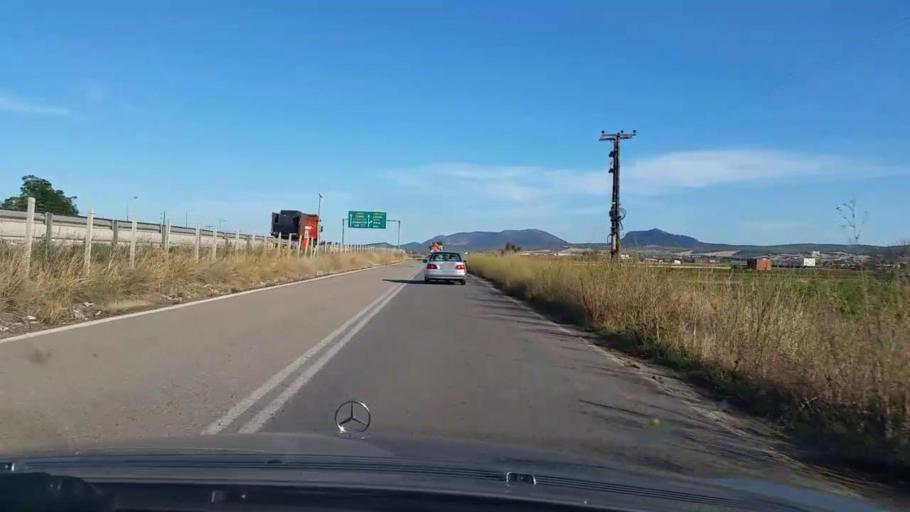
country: GR
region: Central Greece
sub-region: Nomos Voiotias
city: Thivai
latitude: 38.3650
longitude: 23.3110
